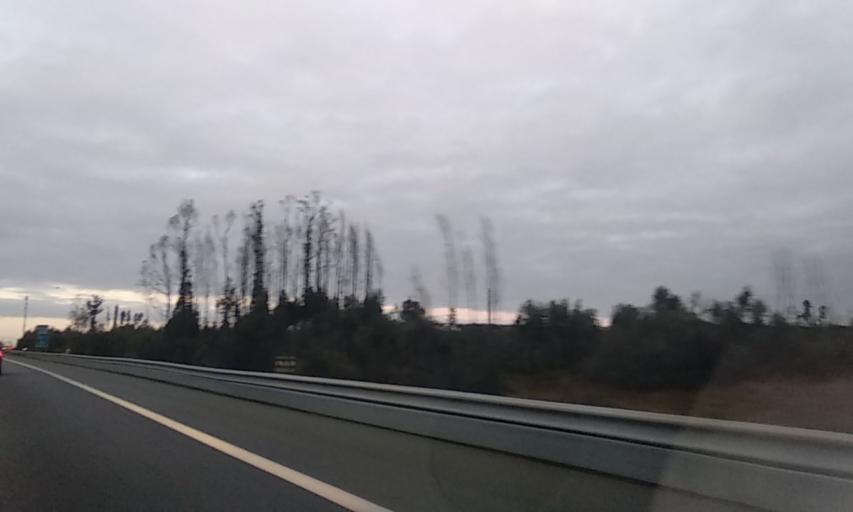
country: PT
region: Aveiro
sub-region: Aveiro
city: Oliveirinha
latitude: 40.5873
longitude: -8.5604
